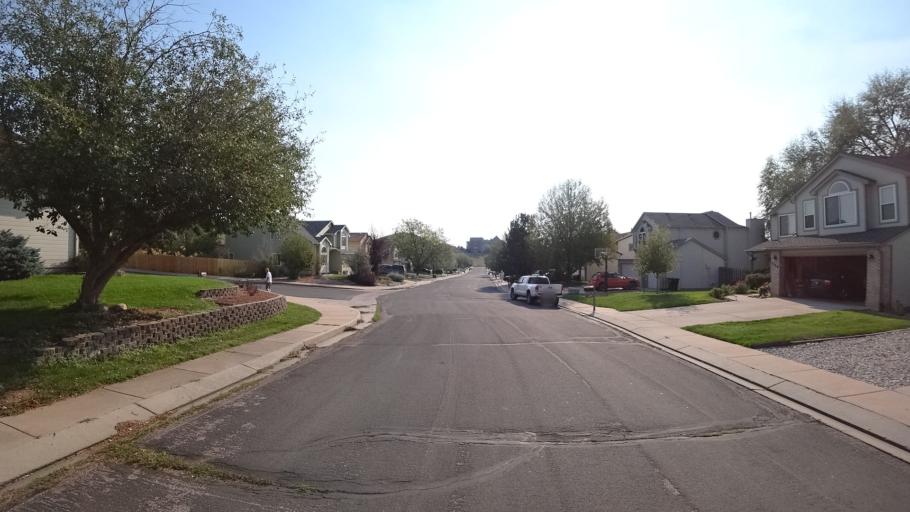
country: US
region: Colorado
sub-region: El Paso County
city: Colorado Springs
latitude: 38.8141
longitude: -104.8491
